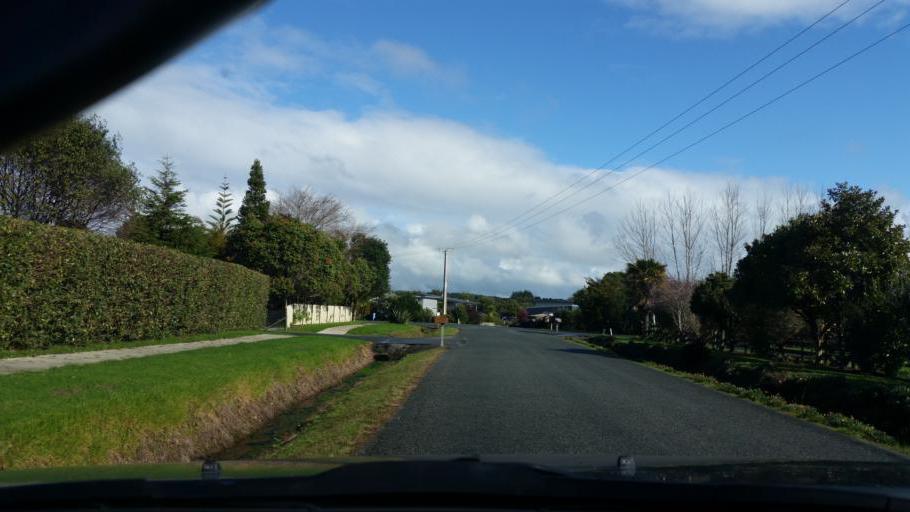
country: NZ
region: Auckland
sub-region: Auckland
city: Wellsford
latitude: -36.0902
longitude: 174.5735
